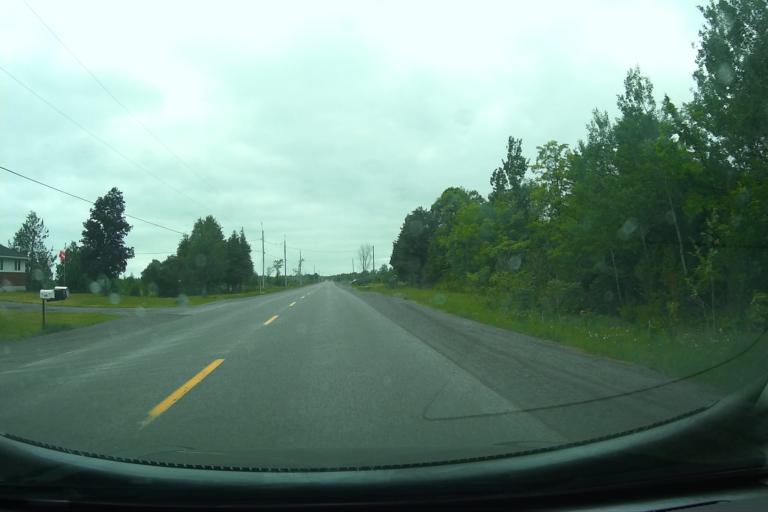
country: CA
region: Ontario
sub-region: Lanark County
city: Smiths Falls
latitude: 45.0378
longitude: -75.8653
